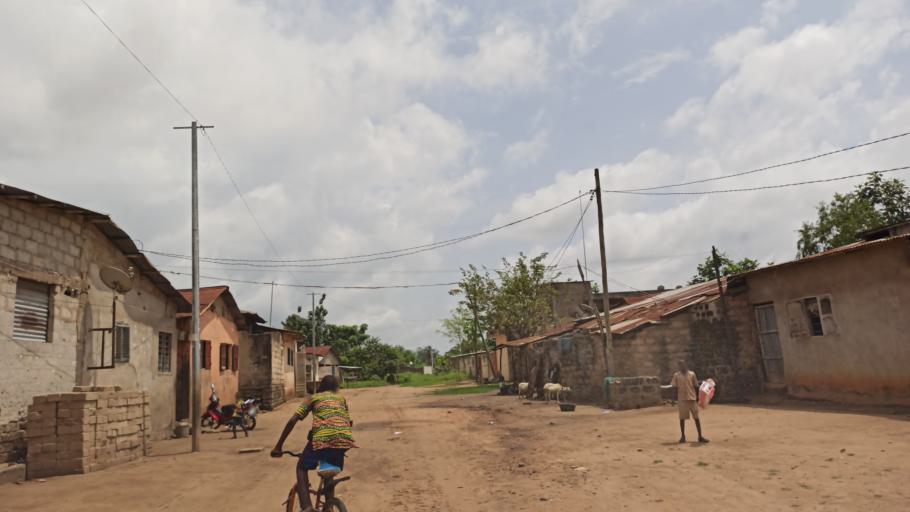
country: BJ
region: Queme
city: Porto-Novo
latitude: 6.4676
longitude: 2.6295
